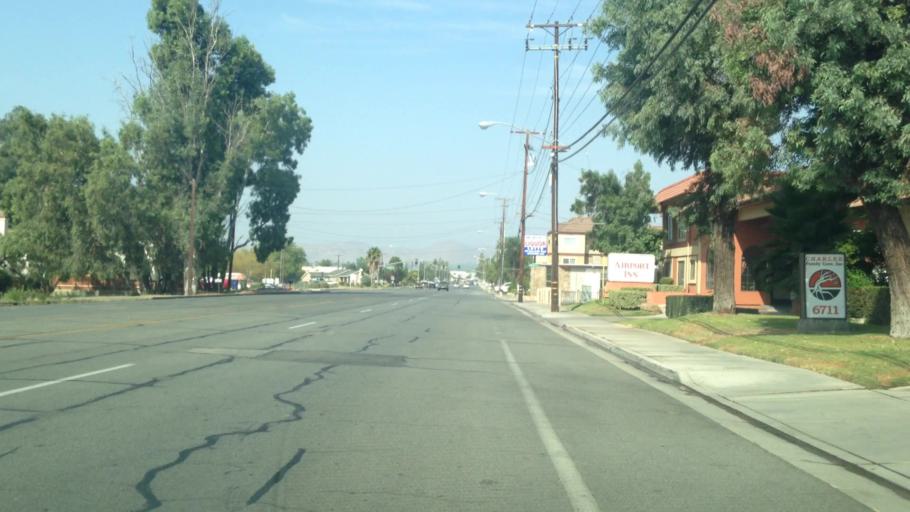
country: US
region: California
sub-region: Riverside County
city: Pedley
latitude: 33.9459
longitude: -117.4427
